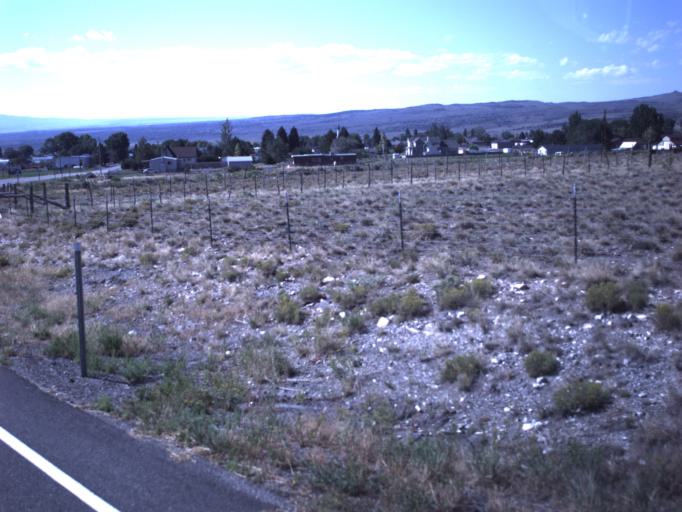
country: US
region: Utah
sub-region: Wayne County
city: Loa
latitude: 38.4121
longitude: -111.6433
